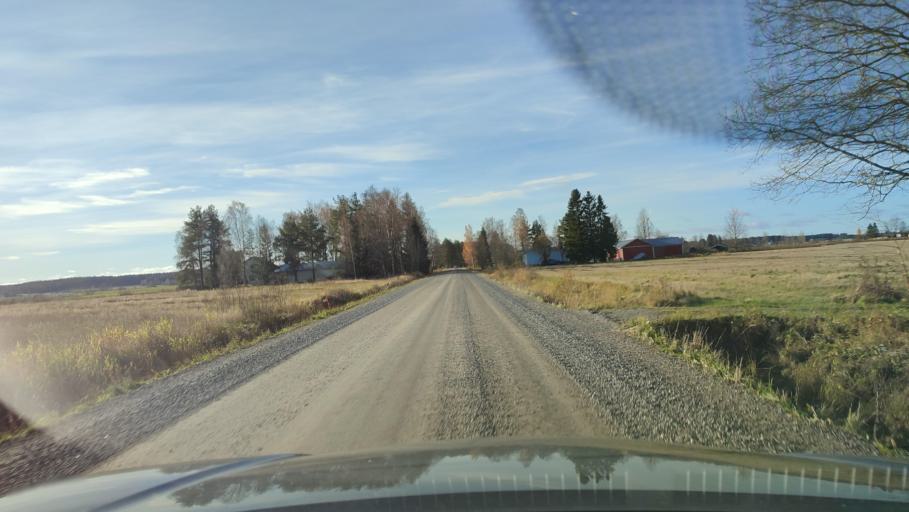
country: FI
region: Southern Ostrobothnia
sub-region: Suupohja
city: Teuva
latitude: 62.4641
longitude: 21.6997
